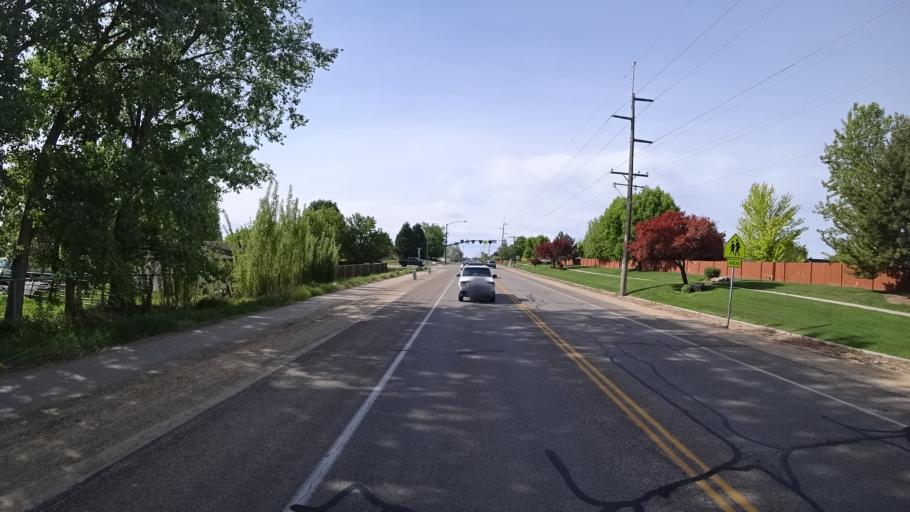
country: US
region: Idaho
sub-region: Ada County
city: Meridian
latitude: 43.5546
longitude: -116.3343
